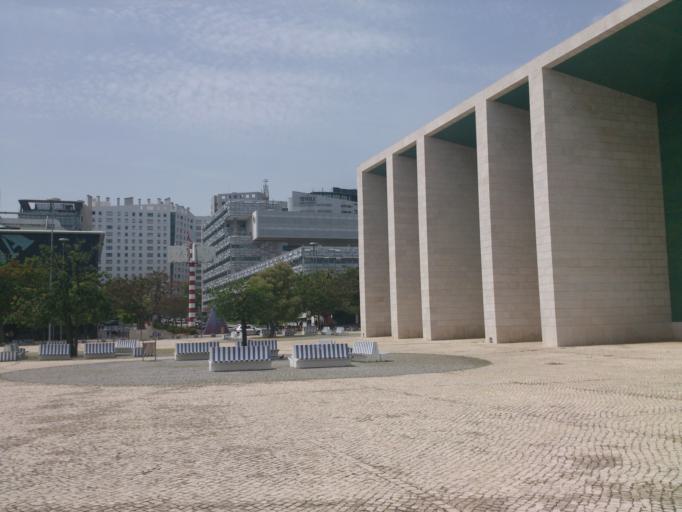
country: PT
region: Lisbon
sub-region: Loures
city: Moscavide
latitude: 38.7653
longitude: -9.0948
